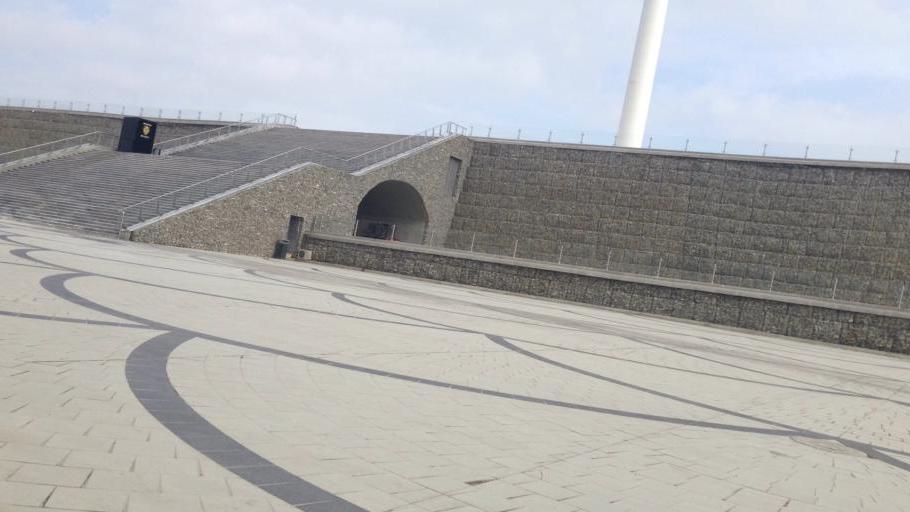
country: AZ
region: Baki
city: Badamdar
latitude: 40.3435
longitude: 49.8439
